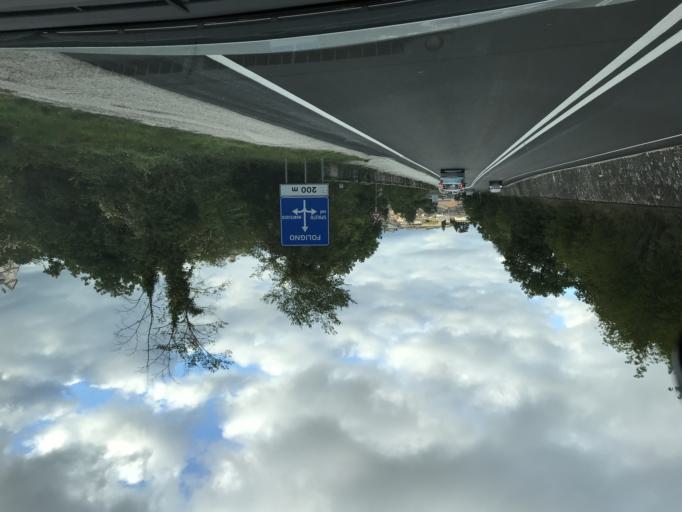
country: IT
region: Umbria
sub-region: Provincia di Perugia
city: Spoleto
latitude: 42.7252
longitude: 12.7347
